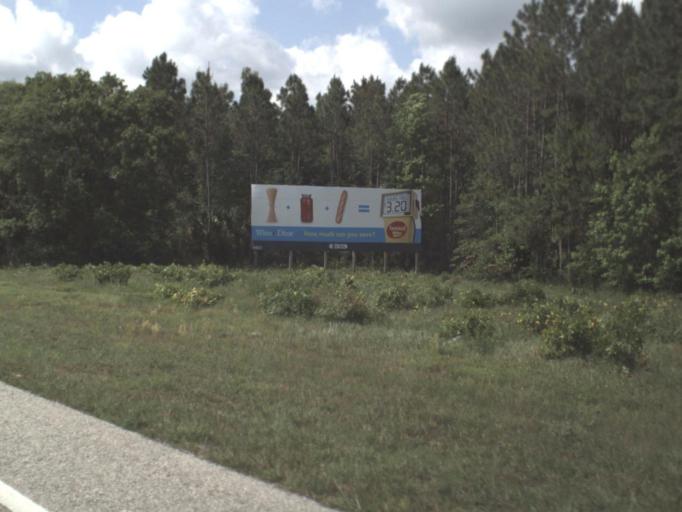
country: US
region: Florida
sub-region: Flagler County
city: Palm Coast
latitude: 29.6715
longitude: -81.2903
